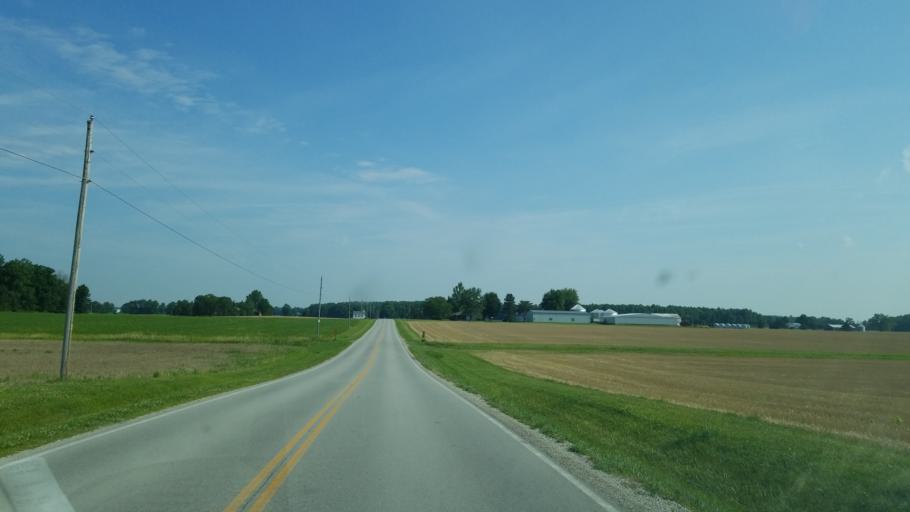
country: US
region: Ohio
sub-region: Huron County
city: Willard
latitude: 41.0013
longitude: -82.8527
